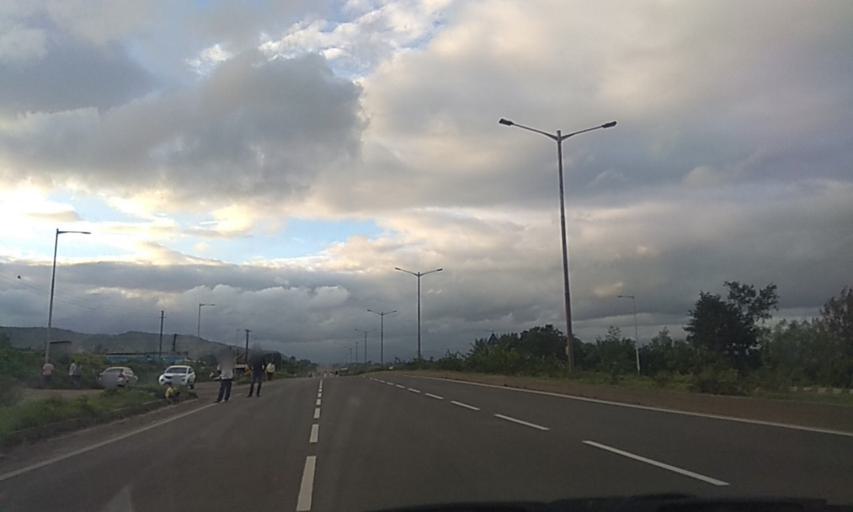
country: IN
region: Maharashtra
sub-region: Satara Division
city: Satara
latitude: 17.7575
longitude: 73.9928
